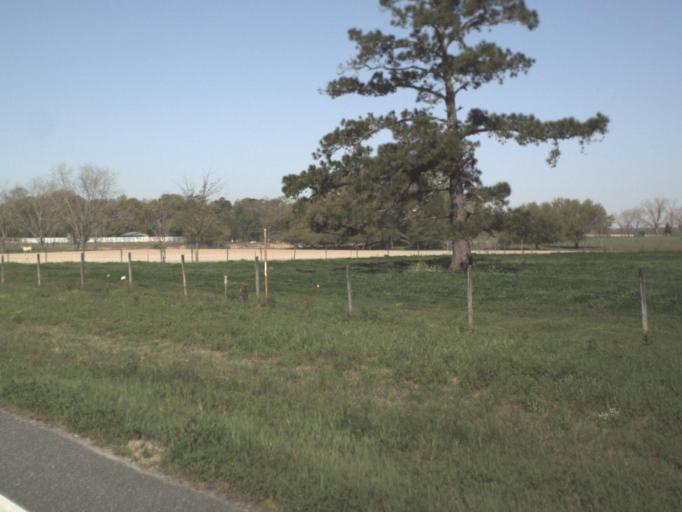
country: US
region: Florida
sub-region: Jackson County
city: Malone
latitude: 30.9543
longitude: -85.2311
